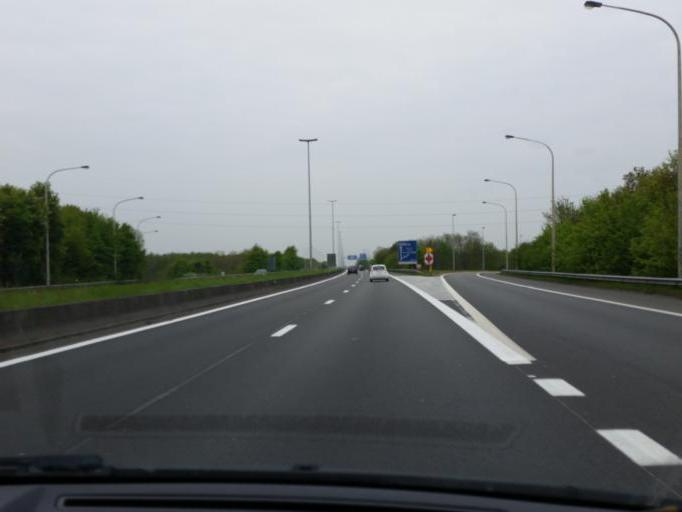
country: BE
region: Flanders
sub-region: Provincie Oost-Vlaanderen
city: Destelbergen
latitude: 51.0455
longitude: 3.8230
